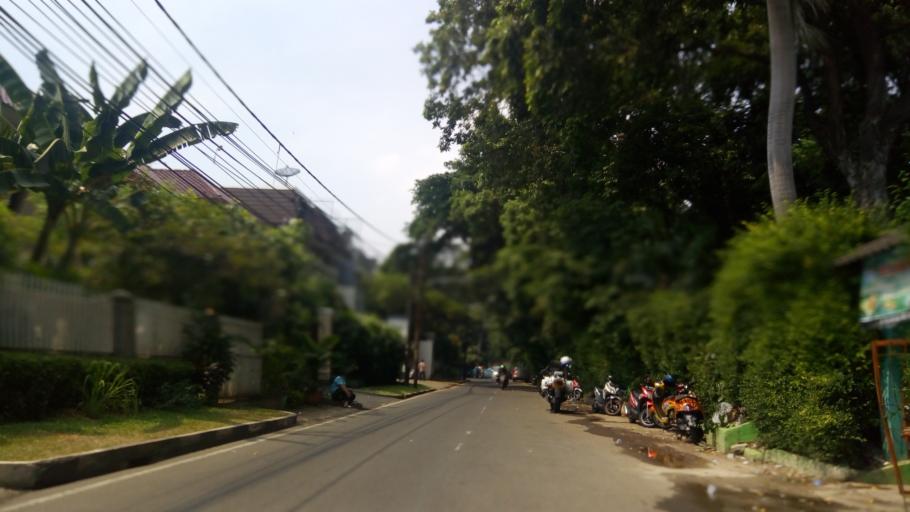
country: ID
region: Jakarta Raya
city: Jakarta
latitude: -6.2006
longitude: 106.8260
